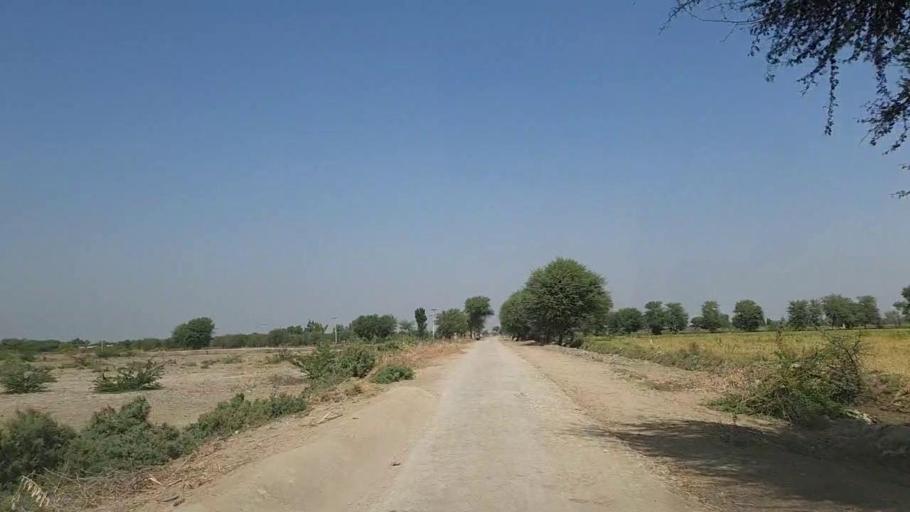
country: PK
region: Sindh
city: Samaro
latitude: 25.2132
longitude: 69.4042
